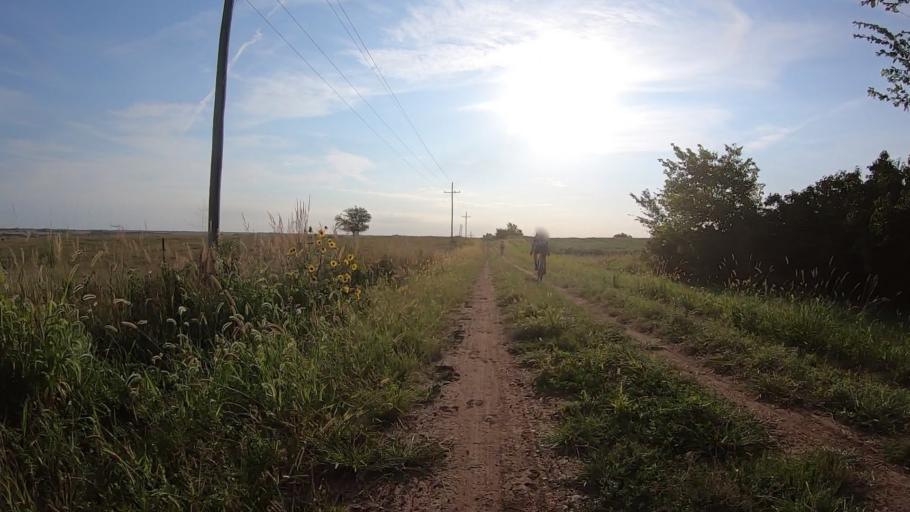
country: US
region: Kansas
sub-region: Marshall County
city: Blue Rapids
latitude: 39.7115
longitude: -96.7972
